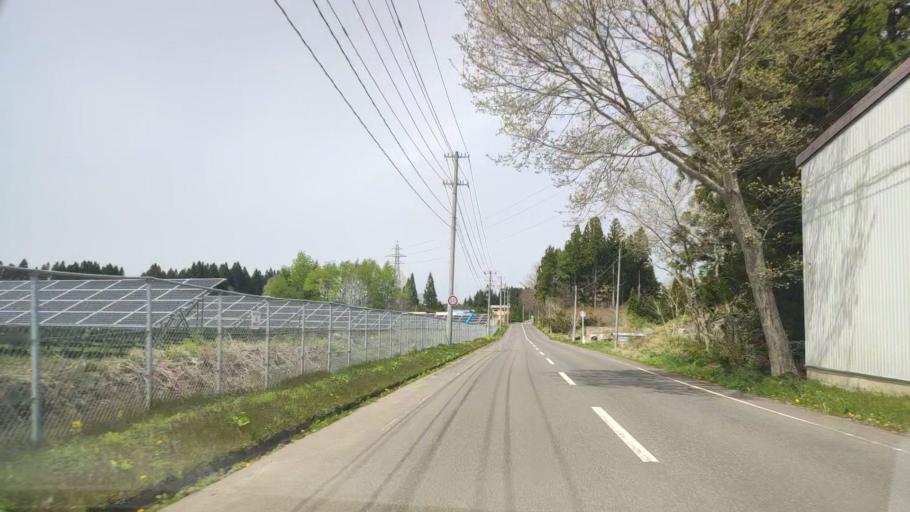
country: JP
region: Aomori
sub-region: Misawa Shi
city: Inuotose
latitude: 40.7206
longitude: 141.1420
